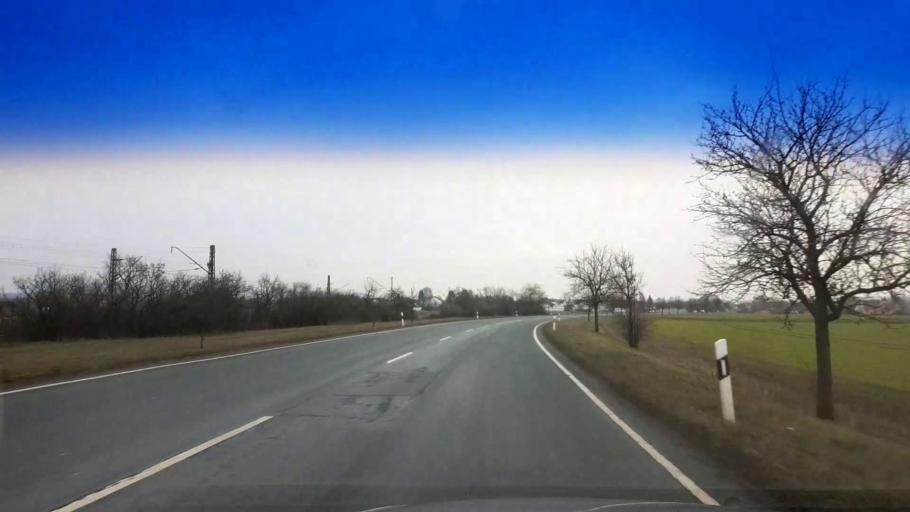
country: DE
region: Bavaria
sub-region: Upper Franconia
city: Altendorf
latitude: 49.8065
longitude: 11.0051
